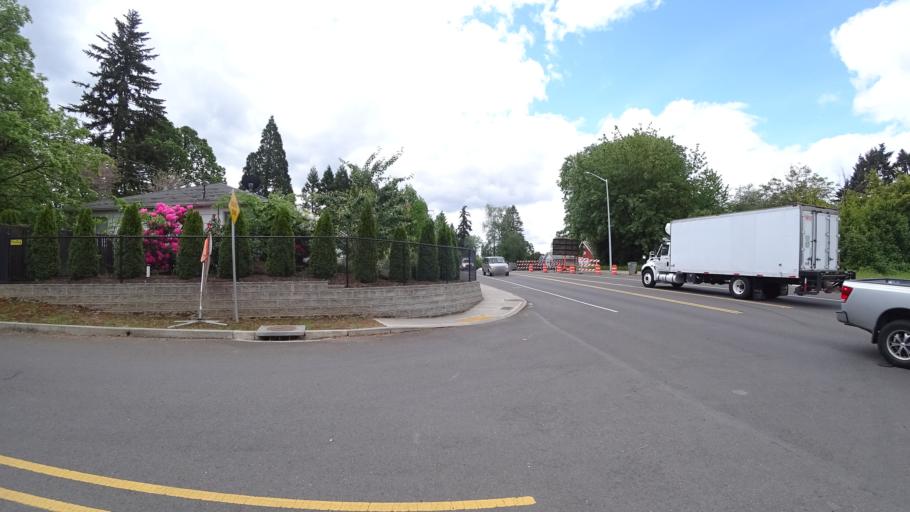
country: US
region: Oregon
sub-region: Washington County
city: Metzger
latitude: 45.4316
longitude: -122.7510
